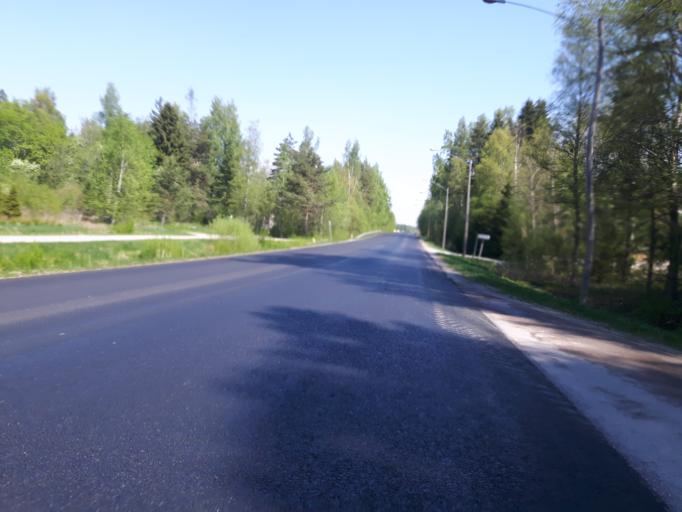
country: FI
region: Uusimaa
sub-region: Helsinki
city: Pornainen
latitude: 60.3363
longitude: 25.4620
